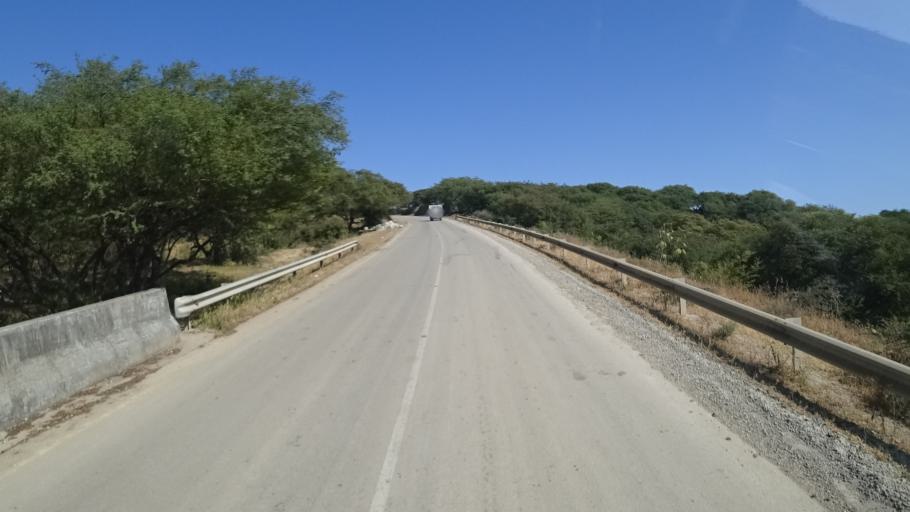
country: OM
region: Zufar
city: Salalah
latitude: 17.0705
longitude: 54.6021
